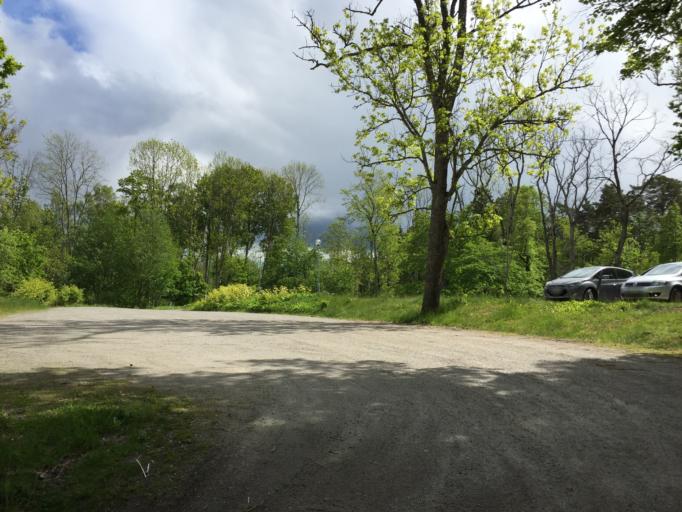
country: SE
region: OEstergoetland
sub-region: Norrkopings Kommun
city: Kimstad
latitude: 58.5520
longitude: 16.0421
